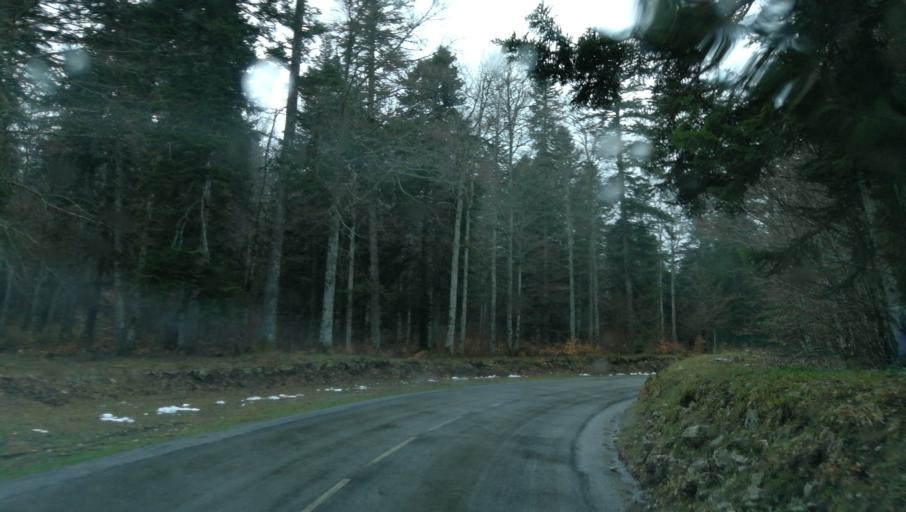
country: FR
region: Rhone-Alpes
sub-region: Departement de la Drome
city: Saint-Jean-en-Royans
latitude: 44.9393
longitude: 5.3089
